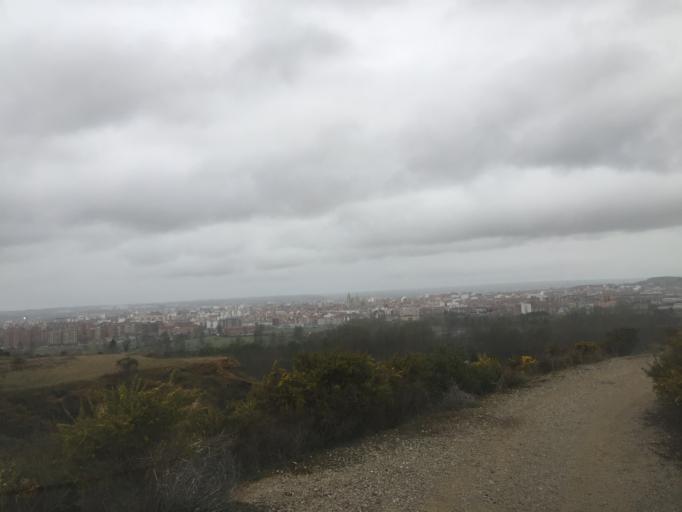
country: ES
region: Castille and Leon
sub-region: Provincia de Leon
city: Leon
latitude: 42.5949
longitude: -5.5425
